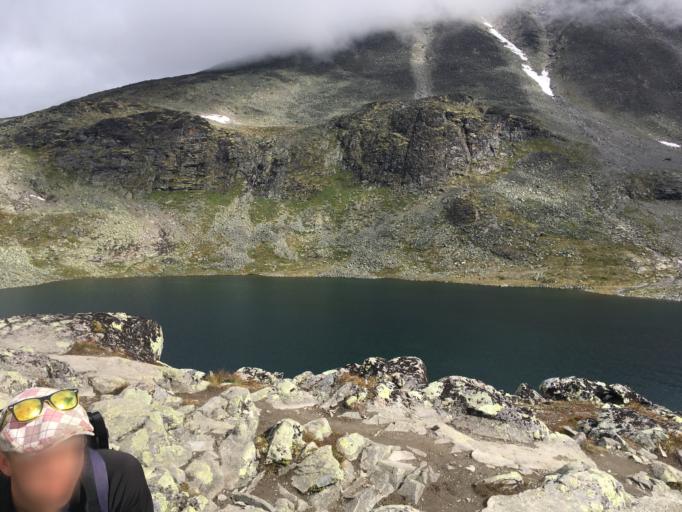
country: NO
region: Oppland
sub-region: Lom
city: Fossbergom
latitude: 61.5018
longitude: 8.6726
